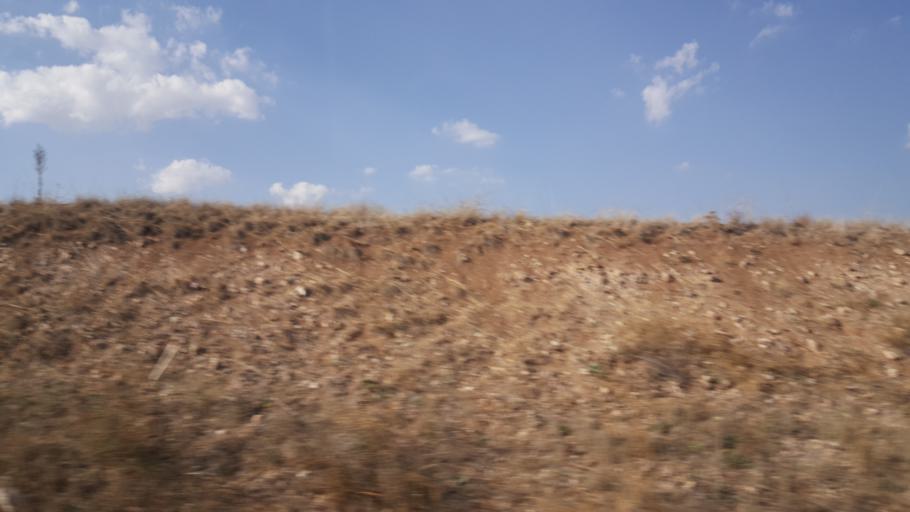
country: TR
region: Eskisehir
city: Kirka
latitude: 39.3178
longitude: 30.5501
